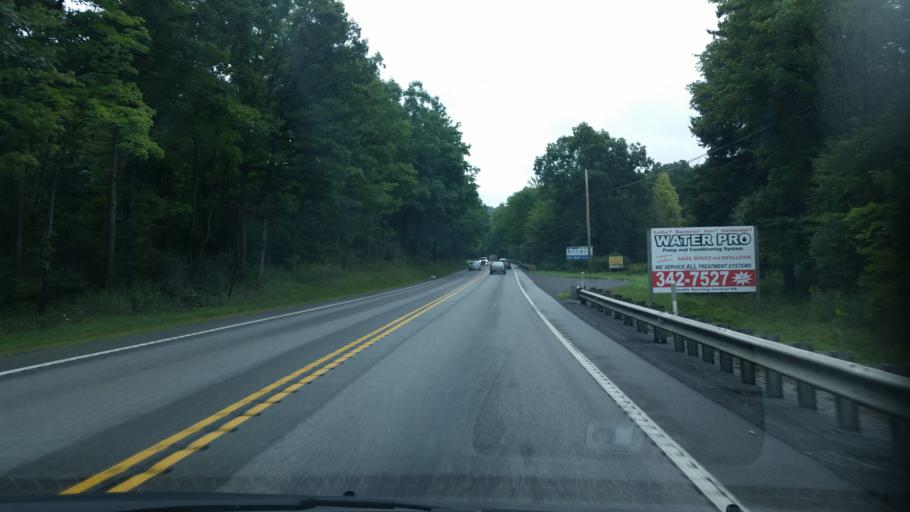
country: US
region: Pennsylvania
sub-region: Clearfield County
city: Troy
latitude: 40.9525
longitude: -78.2925
